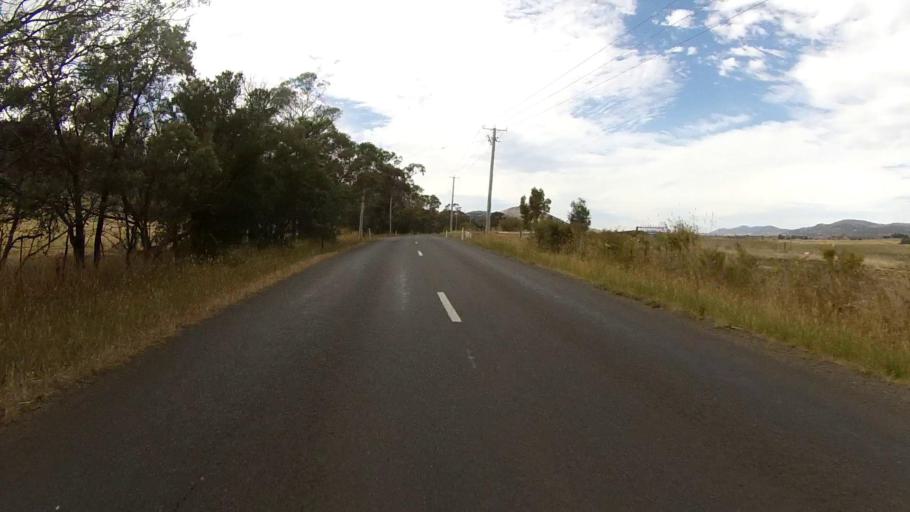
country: AU
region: Tasmania
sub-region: Clarence
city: Cambridge
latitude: -42.7212
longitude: 147.3927
